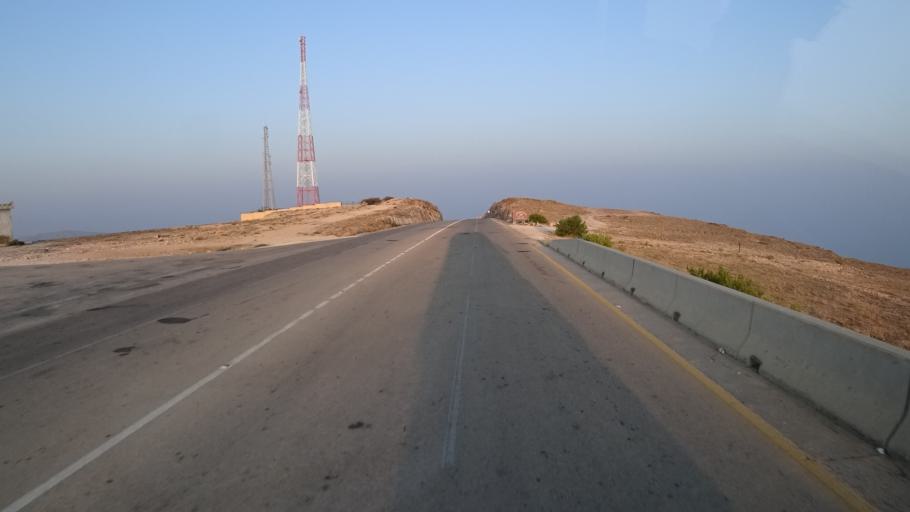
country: OM
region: Zufar
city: Salalah
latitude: 16.8256
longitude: 53.6503
